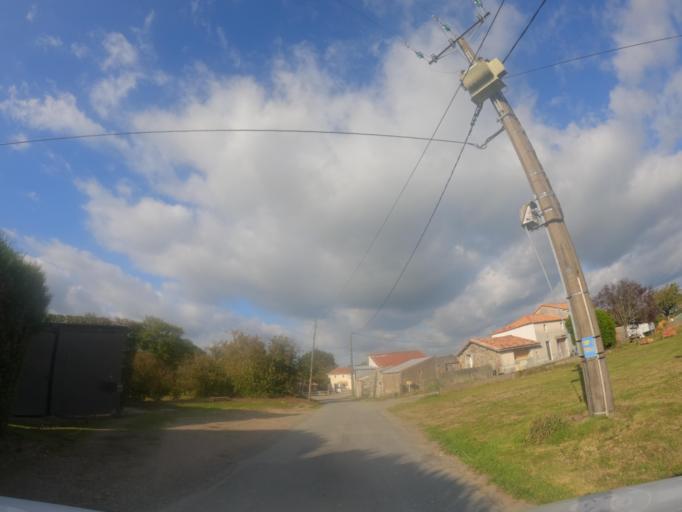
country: FR
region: Poitou-Charentes
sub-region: Departement des Deux-Sevres
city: La Foret-sur-Sevre
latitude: 46.7860
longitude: -0.6295
